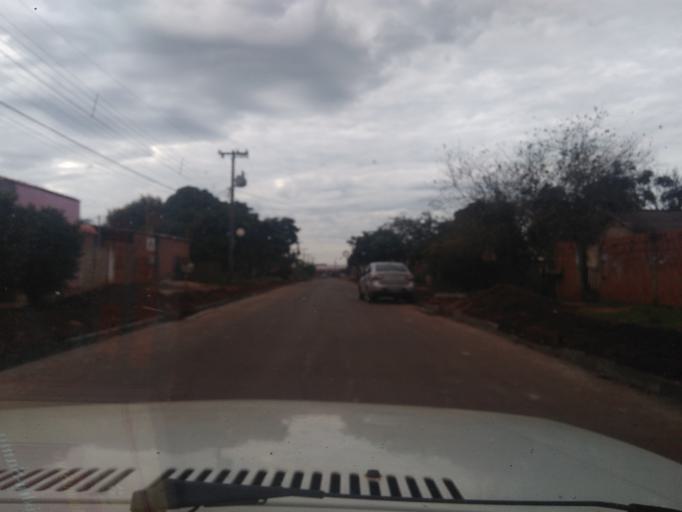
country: BR
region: Mato Grosso do Sul
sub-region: Ponta Pora
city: Ponta Pora
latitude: -22.5095
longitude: -55.7331
